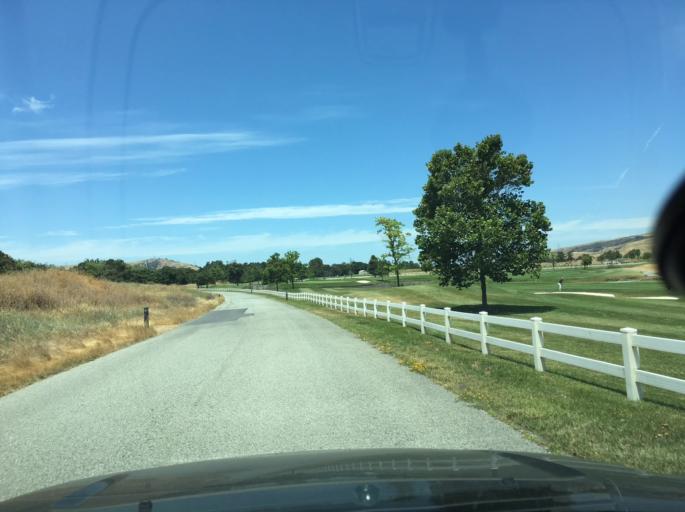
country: US
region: California
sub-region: Santa Clara County
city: Morgan Hill
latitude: 37.1898
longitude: -121.7021
